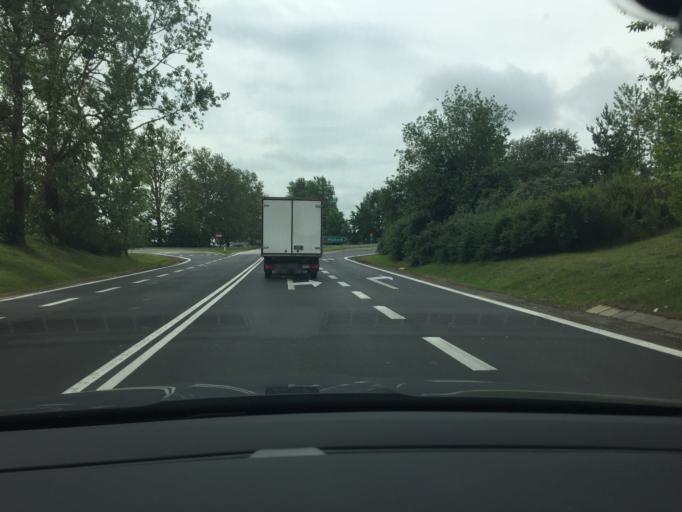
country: PL
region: Pomeranian Voivodeship
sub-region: Powiat tczewski
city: Subkowy
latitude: 54.0483
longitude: 18.7610
